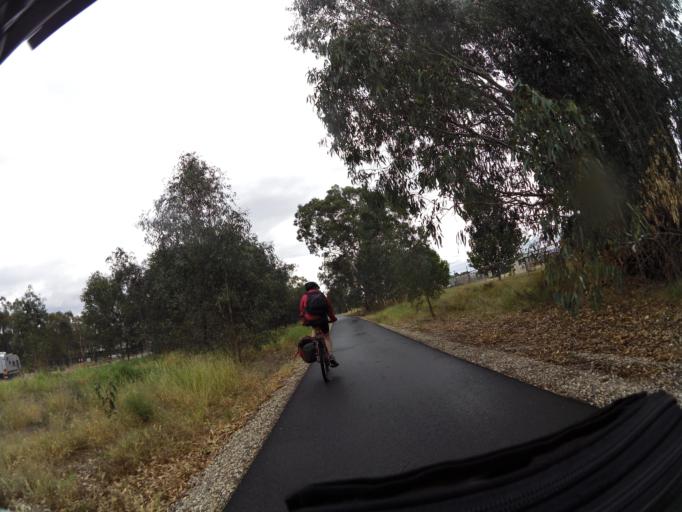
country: AU
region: Victoria
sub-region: Wodonga
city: Wodonga
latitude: -36.1368
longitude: 146.9046
